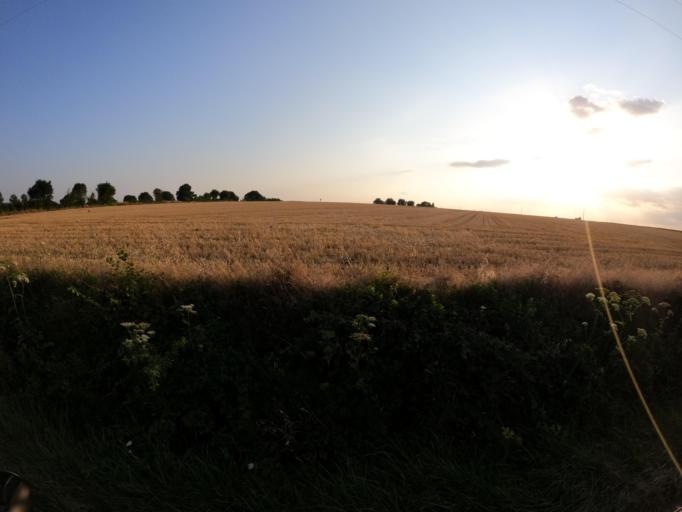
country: FR
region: Pays de la Loire
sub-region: Departement de la Sarthe
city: Brulon
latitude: 47.9160
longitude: -0.2285
